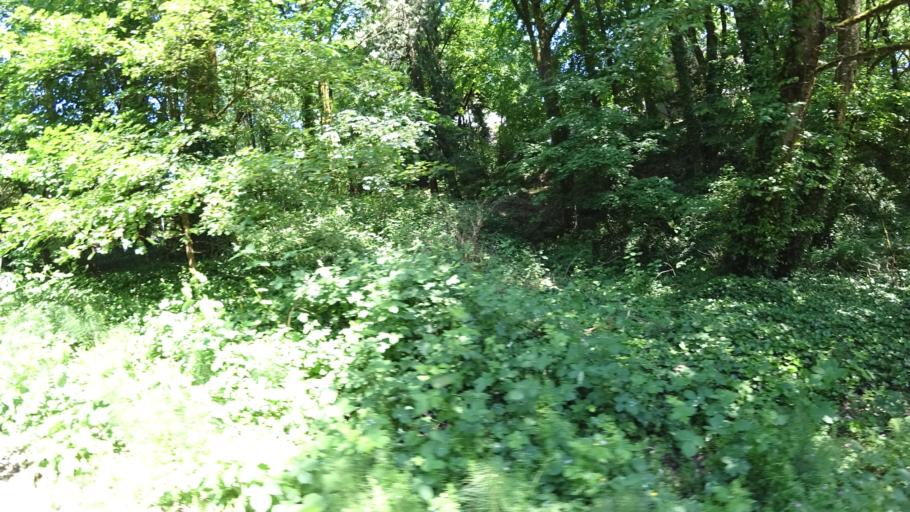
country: US
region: Oregon
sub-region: Multnomah County
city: Portland
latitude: 45.4948
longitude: -122.7044
